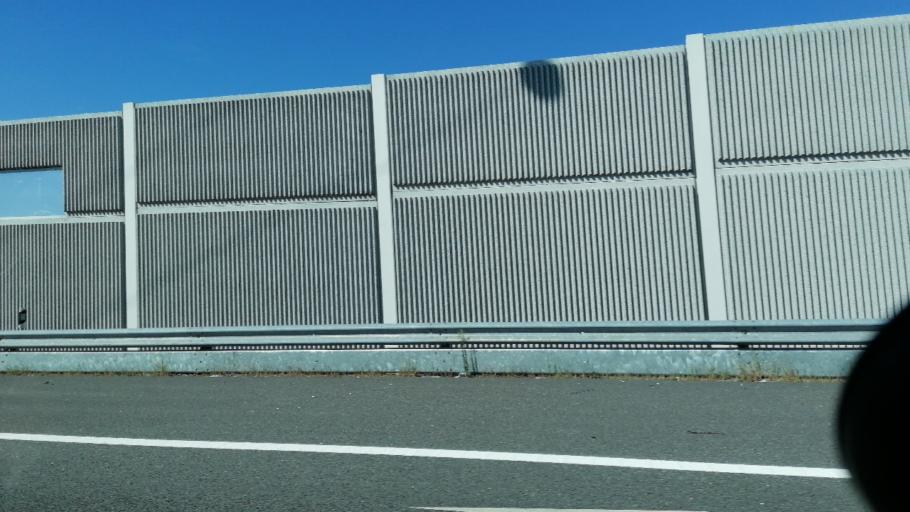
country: PT
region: Porto
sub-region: Vila Nova de Gaia
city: Vilar de Andorinho
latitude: 41.0985
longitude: -8.5941
